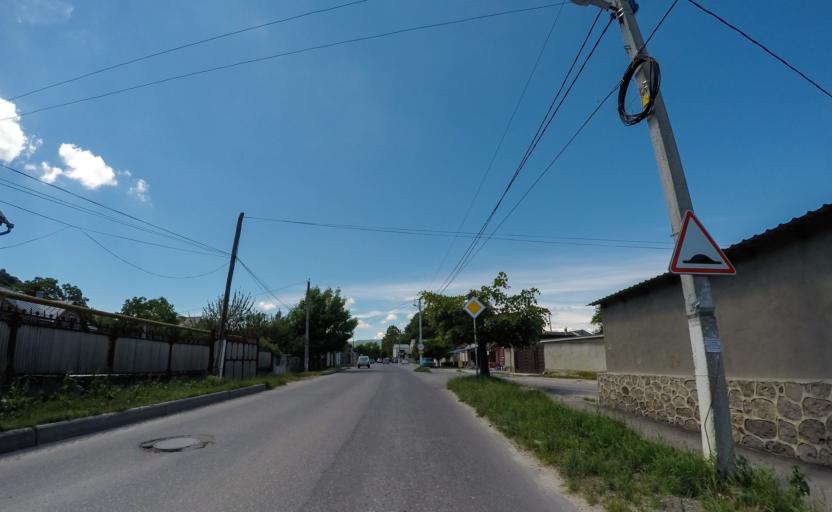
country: RU
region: Kabardino-Balkariya
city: Belaya Rechka
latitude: 43.4436
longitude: 43.5838
